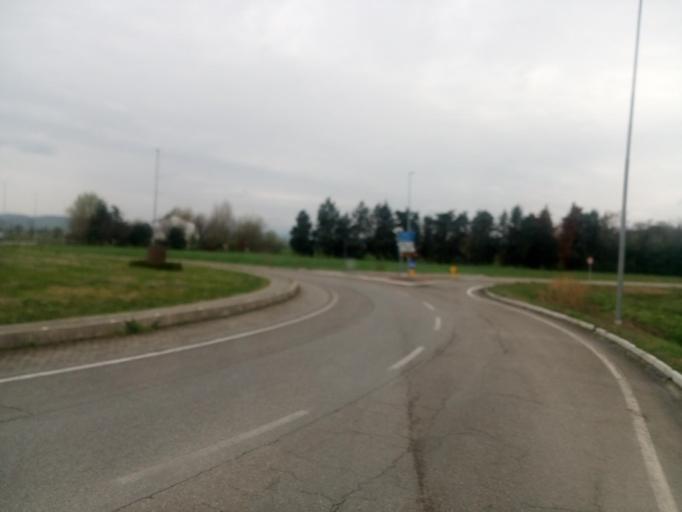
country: IT
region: Emilia-Romagna
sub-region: Forli-Cesena
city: Fratta Terme
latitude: 44.1760
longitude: 12.0779
